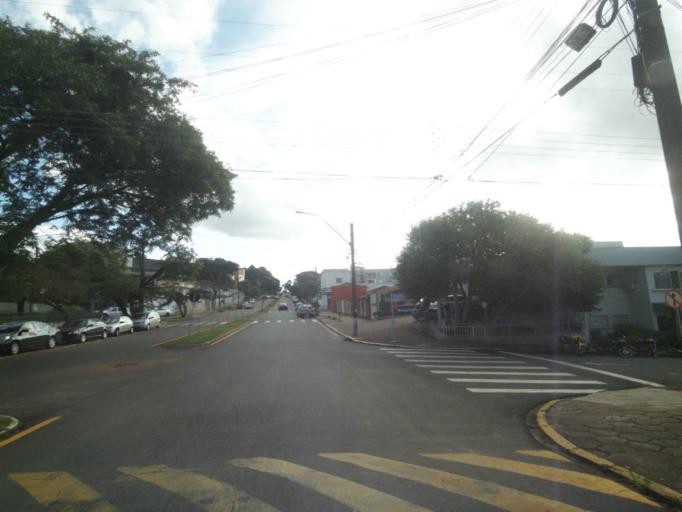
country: BR
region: Parana
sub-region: Telemaco Borba
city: Telemaco Borba
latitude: -24.3268
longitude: -50.6177
